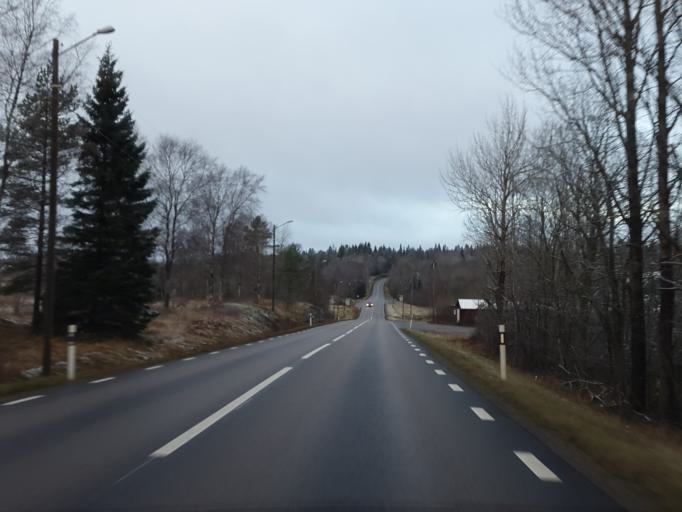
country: SE
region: Vaestra Goetaland
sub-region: Boras Kommun
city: Sandared
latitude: 57.8309
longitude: 12.7076
